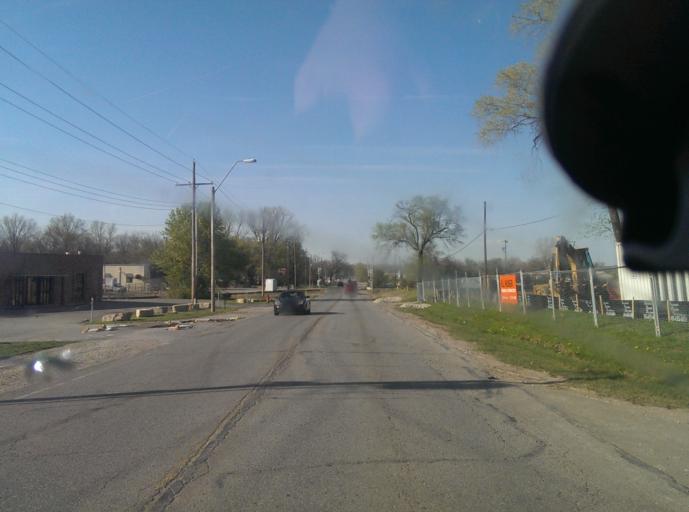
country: US
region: Missouri
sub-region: Jackson County
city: Grandview
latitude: 38.8844
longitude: -94.5864
